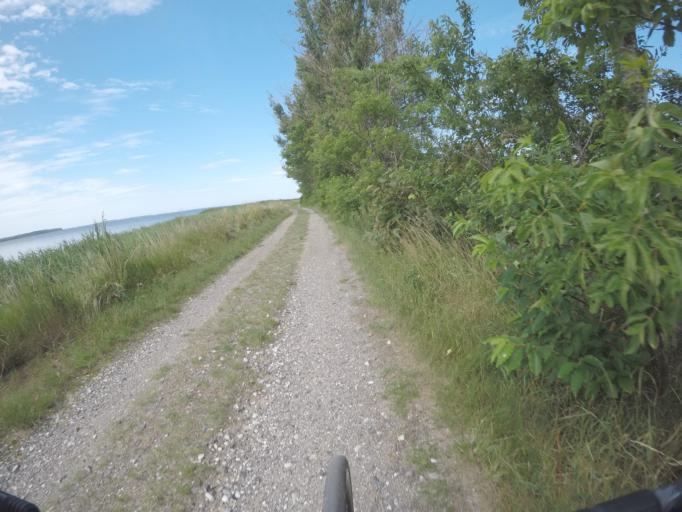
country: DE
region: Mecklenburg-Vorpommern
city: Altefahr
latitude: 54.3607
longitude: 13.1232
